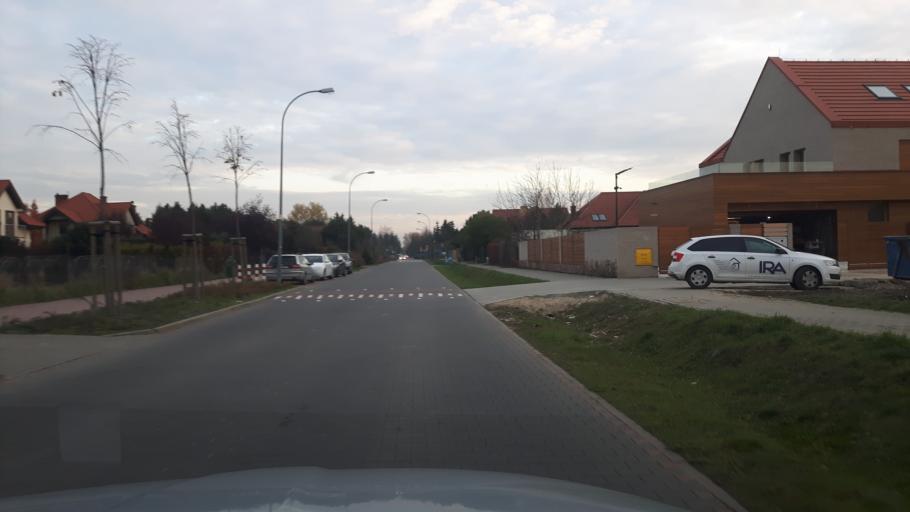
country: PL
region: Masovian Voivodeship
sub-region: Warszawa
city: Wilanow
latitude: 52.1761
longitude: 21.1098
